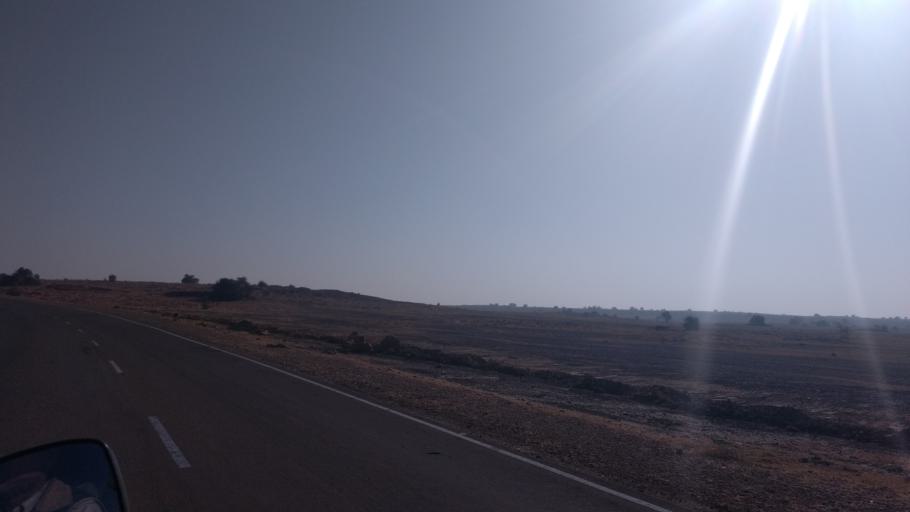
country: IN
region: Rajasthan
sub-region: Jaisalmer
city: Jaisalmer
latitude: 26.9082
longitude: 70.7405
